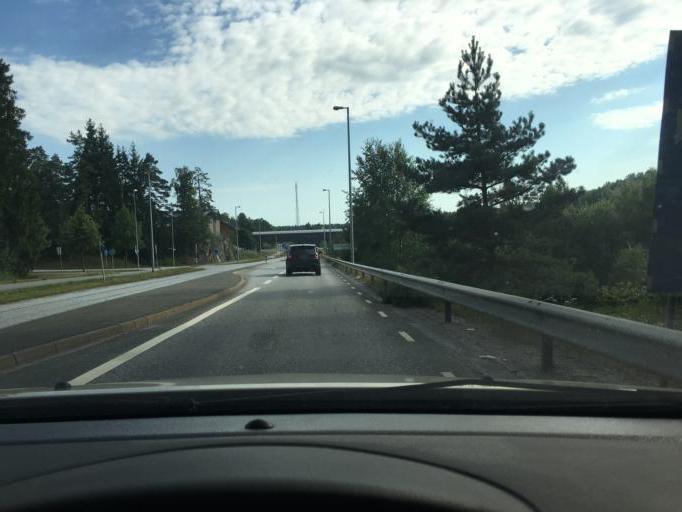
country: SE
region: Stockholm
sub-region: Sodertalje Kommun
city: Pershagen
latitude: 59.1612
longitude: 17.6420
